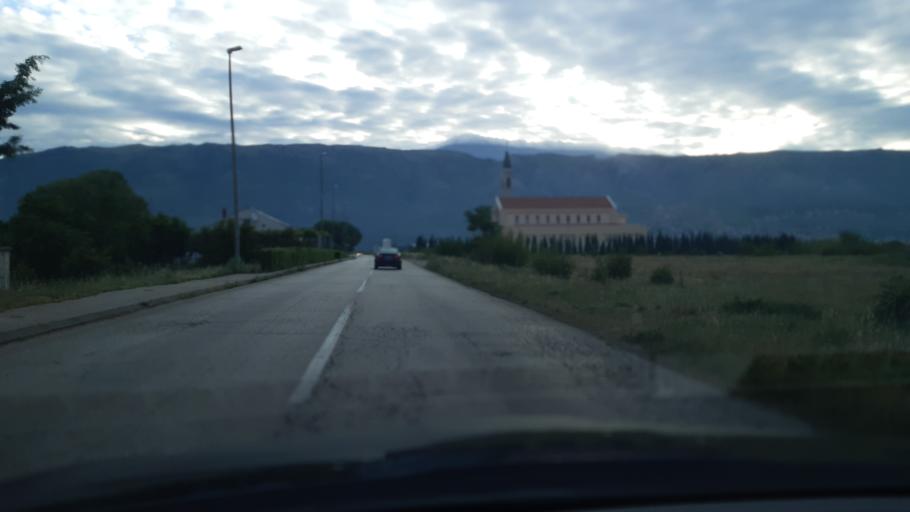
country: BA
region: Federation of Bosnia and Herzegovina
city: Rodoc
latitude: 43.3112
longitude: 17.8113
